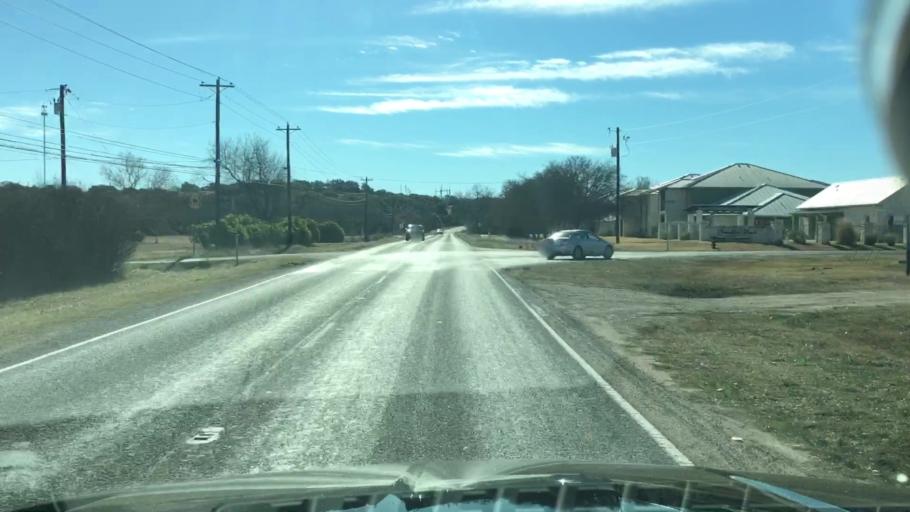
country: US
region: Texas
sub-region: Blanco County
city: Blanco
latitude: 30.0901
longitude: -98.4154
